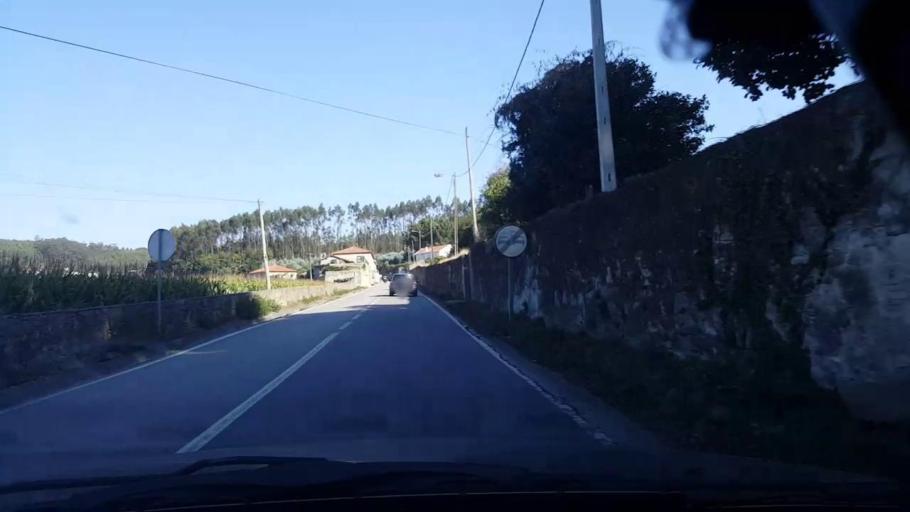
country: PT
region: Porto
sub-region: Maia
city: Gemunde
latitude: 41.3260
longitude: -8.6549
